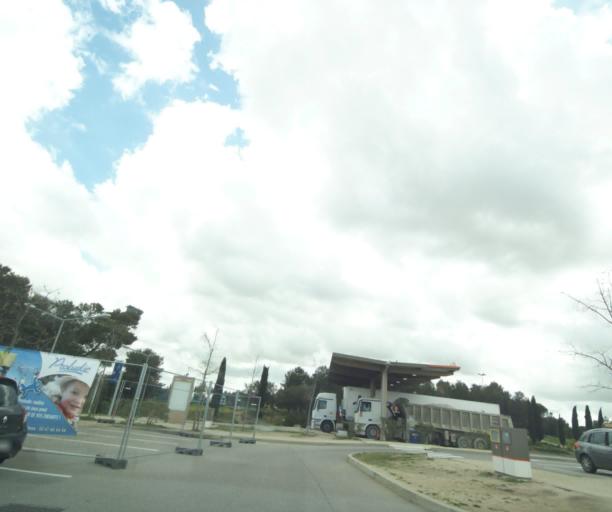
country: FR
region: Languedoc-Roussillon
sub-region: Departement de l'Herault
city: Villetelle
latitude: 43.7124
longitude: 4.1322
